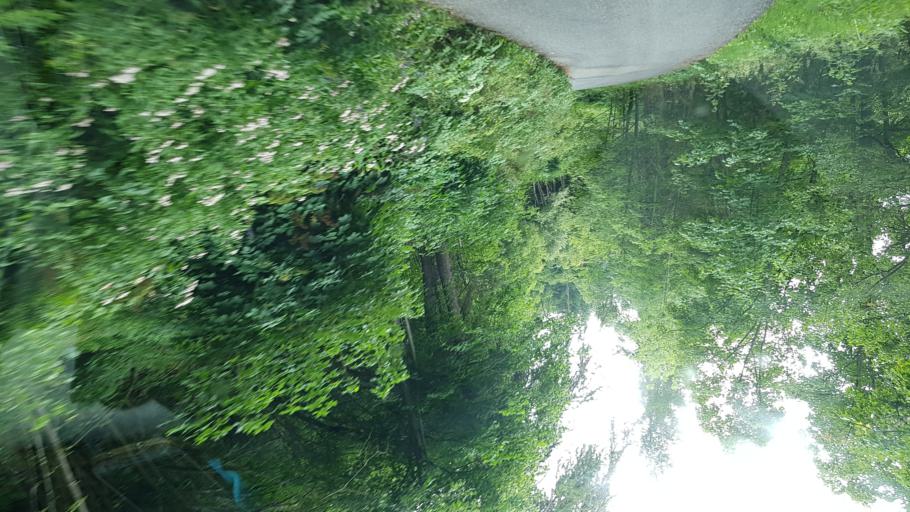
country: IT
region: Piedmont
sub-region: Provincia di Cuneo
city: Stroppo
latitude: 44.5127
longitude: 7.1123
